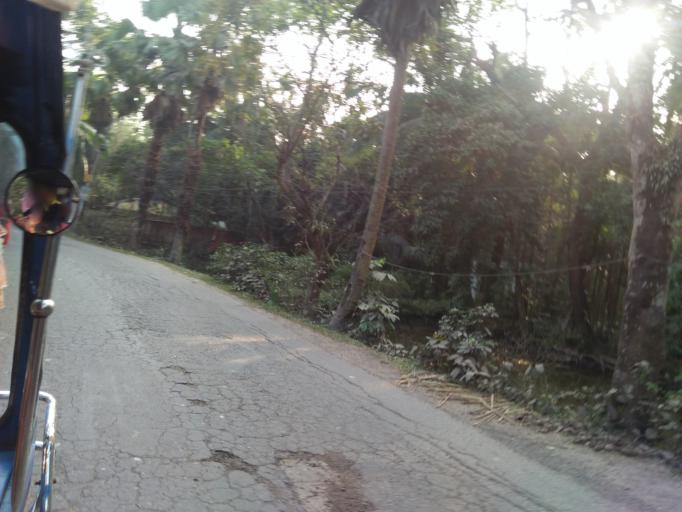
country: BD
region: Barisal
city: Bhola
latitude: 22.7025
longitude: 90.6413
